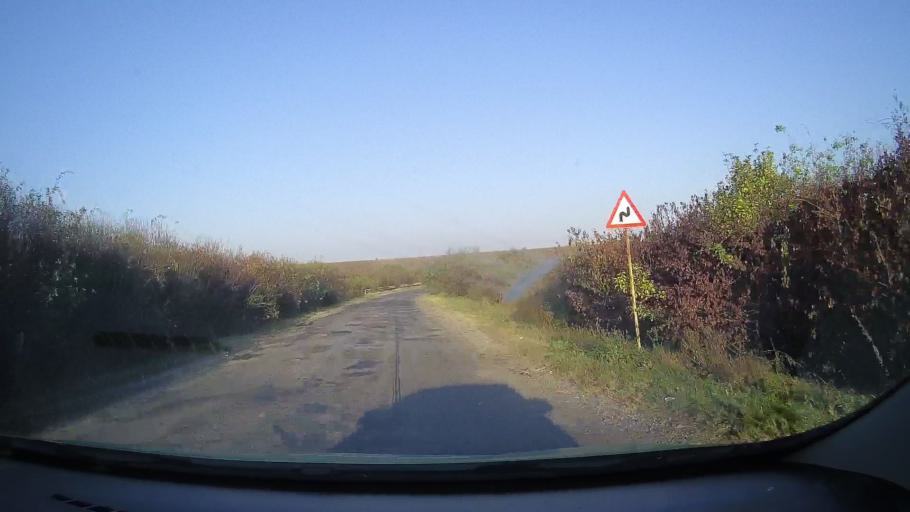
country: RO
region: Arad
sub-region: Comuna Pancota
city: Maderat
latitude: 46.3114
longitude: 21.7454
